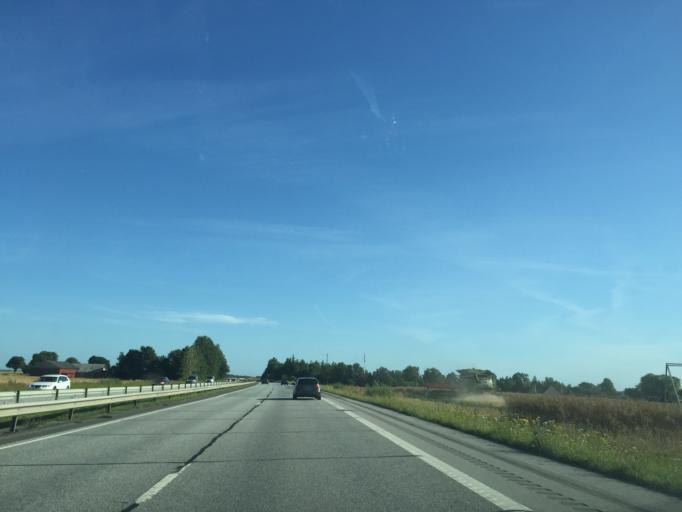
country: SE
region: Skane
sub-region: Malmo
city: Tygelsjo
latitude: 55.5204
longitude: 13.0093
